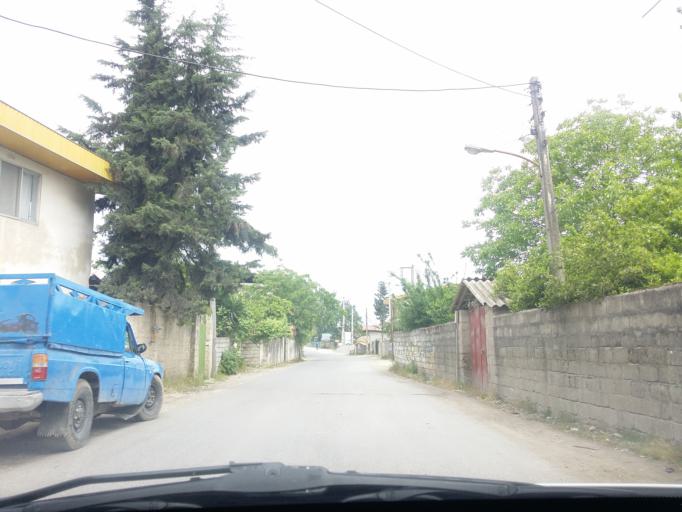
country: IR
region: Mazandaran
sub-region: Nowshahr
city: Nowshahr
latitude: 36.6242
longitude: 51.4927
